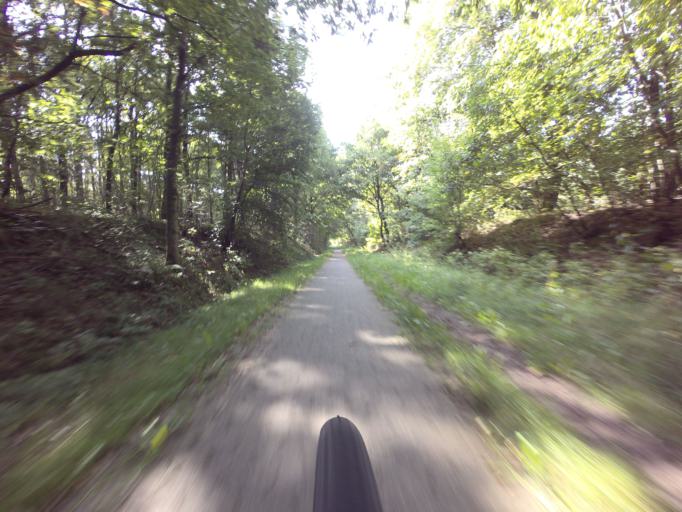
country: DK
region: Central Jutland
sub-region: Viborg Kommune
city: Viborg
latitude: 56.3900
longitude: 9.3024
